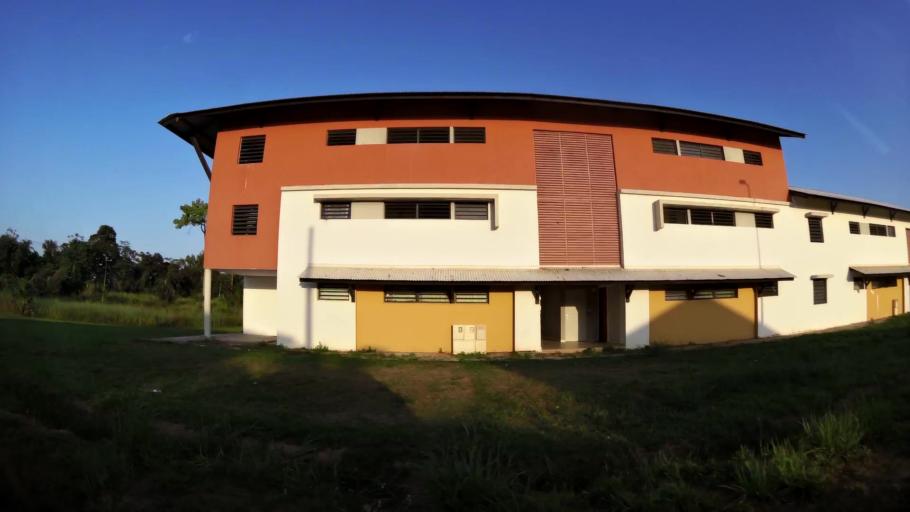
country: GF
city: Macouria
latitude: 5.0085
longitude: -52.4681
